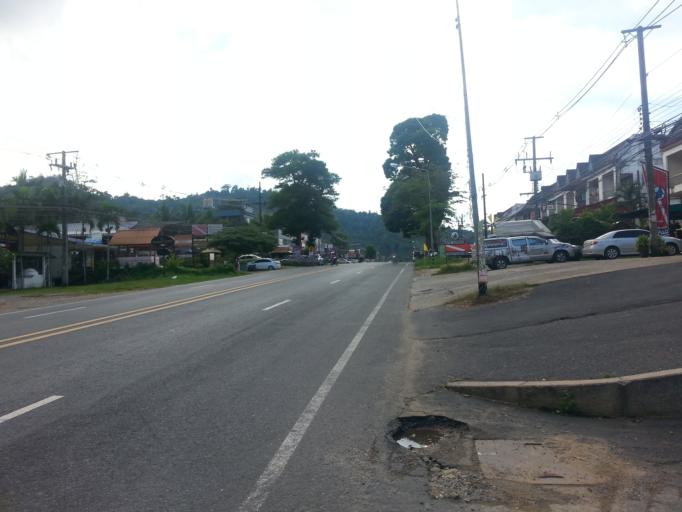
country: TH
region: Phangnga
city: Ban Khao Lak
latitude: 8.6501
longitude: 98.2526
